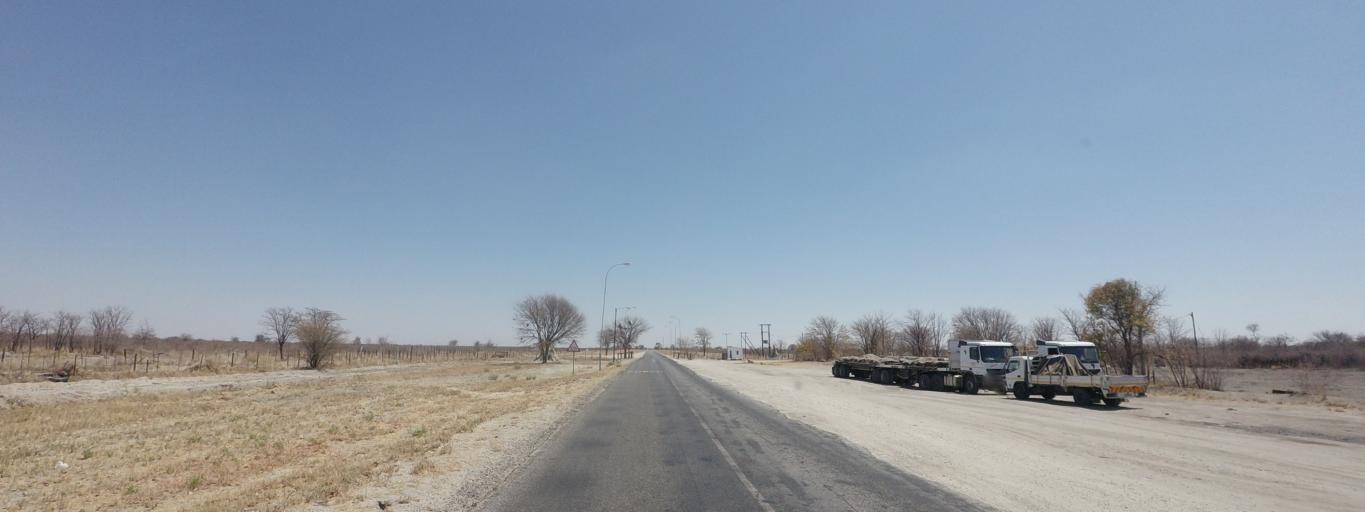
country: BW
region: Central
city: Nata
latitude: -20.3159
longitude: 26.3084
